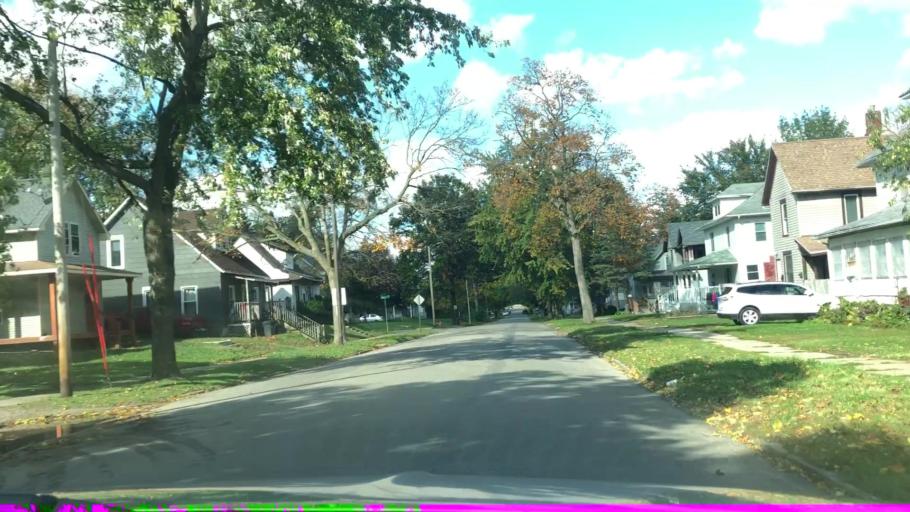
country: US
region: Iowa
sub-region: Marshall County
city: Marshalltown
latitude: 42.0533
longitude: -92.9179
